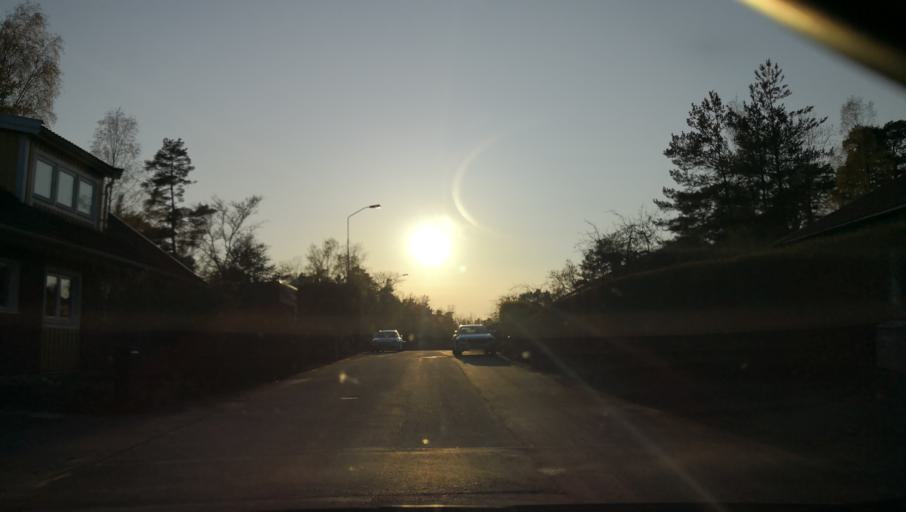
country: SE
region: Stockholm
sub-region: Varmdo Kommun
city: Hemmesta
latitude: 59.3220
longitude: 18.5036
